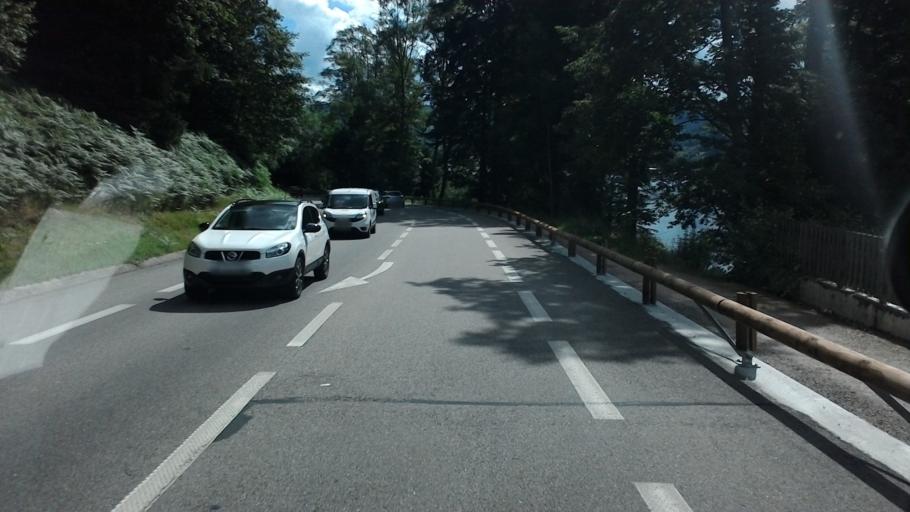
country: FR
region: Lorraine
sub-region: Departement des Vosges
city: Gerardmer
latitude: 48.0725
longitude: 6.8419
